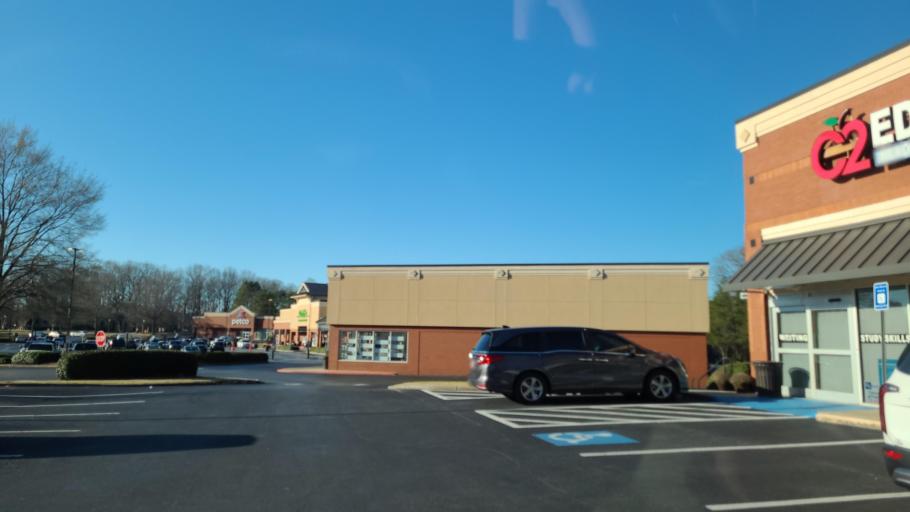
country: US
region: Georgia
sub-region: Fulton County
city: Sandy Springs
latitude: 33.9761
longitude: -84.4141
